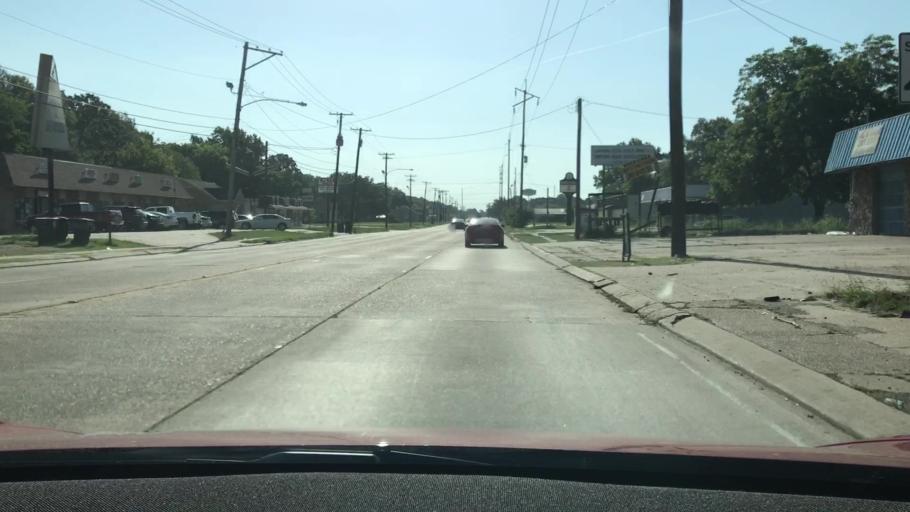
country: US
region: Louisiana
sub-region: Bossier Parish
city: Bossier City
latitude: 32.4420
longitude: -93.7708
